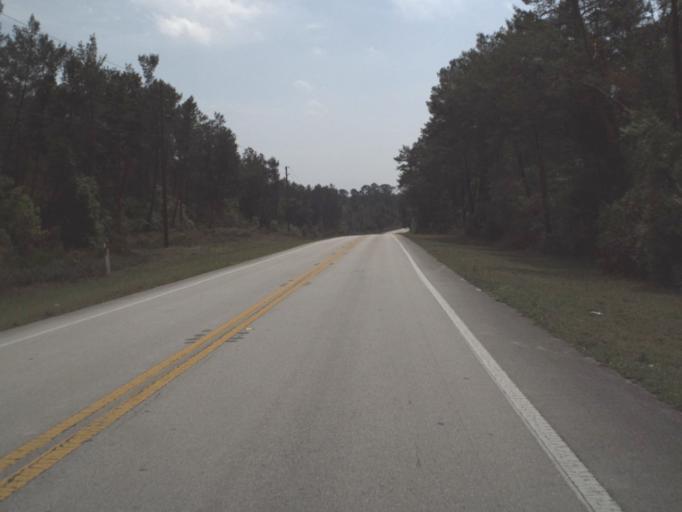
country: US
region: Florida
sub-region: Putnam County
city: Crescent City
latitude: 29.3330
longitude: -81.7160
